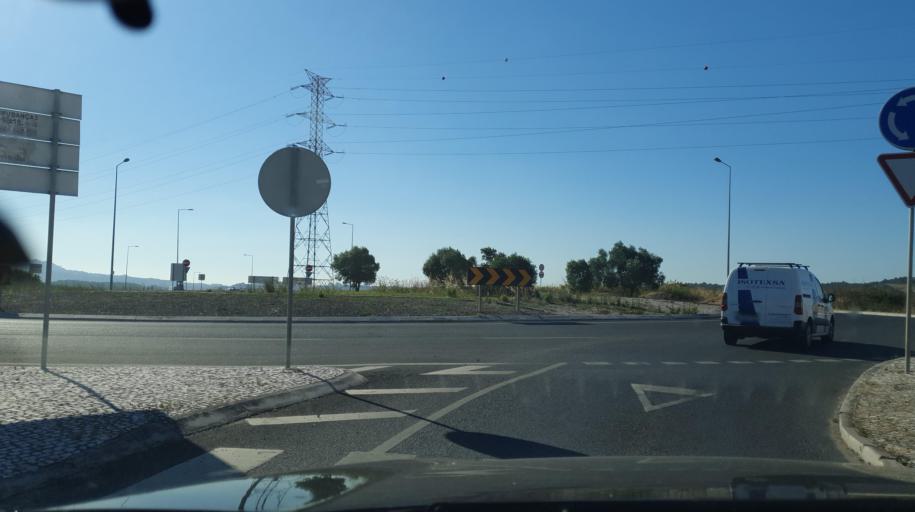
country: PT
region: Lisbon
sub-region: Sintra
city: Cacem
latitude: 38.7693
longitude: -9.2796
